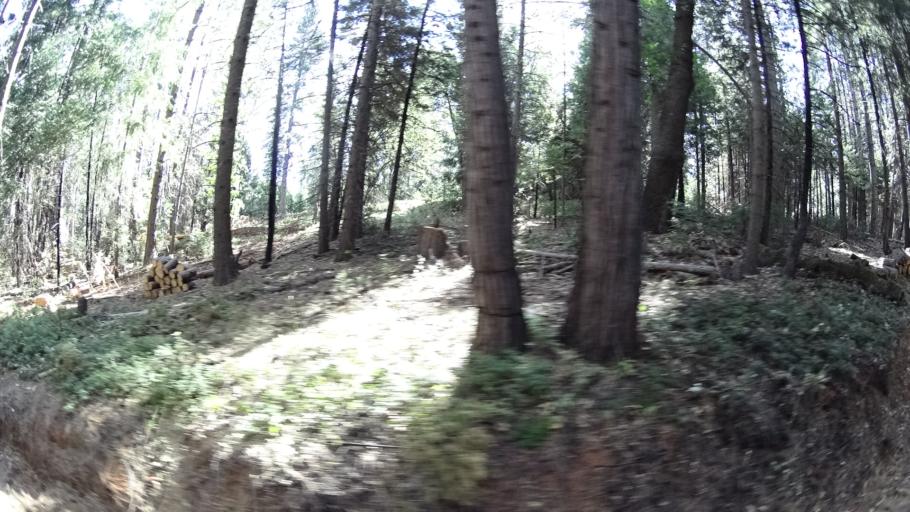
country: US
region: California
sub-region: Amador County
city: Pioneer
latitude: 38.3832
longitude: -120.4522
